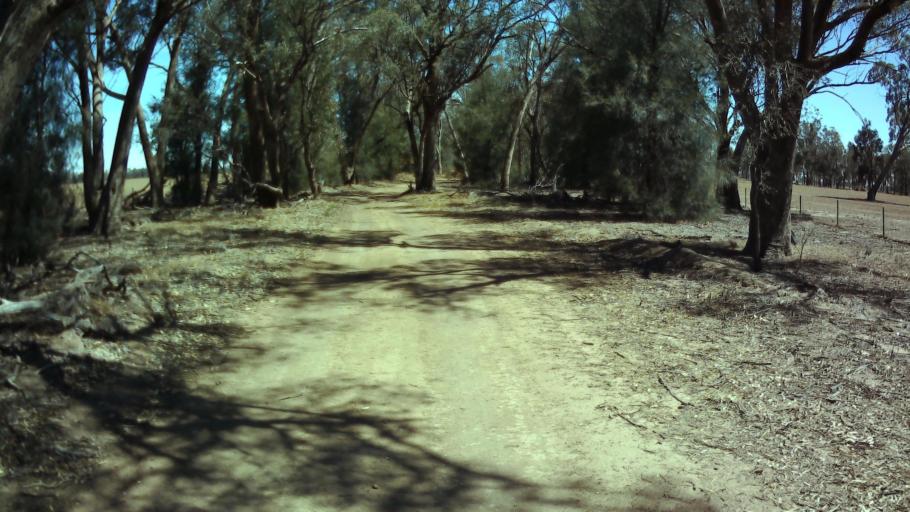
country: AU
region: New South Wales
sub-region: Bland
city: West Wyalong
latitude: -33.9144
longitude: 147.6839
